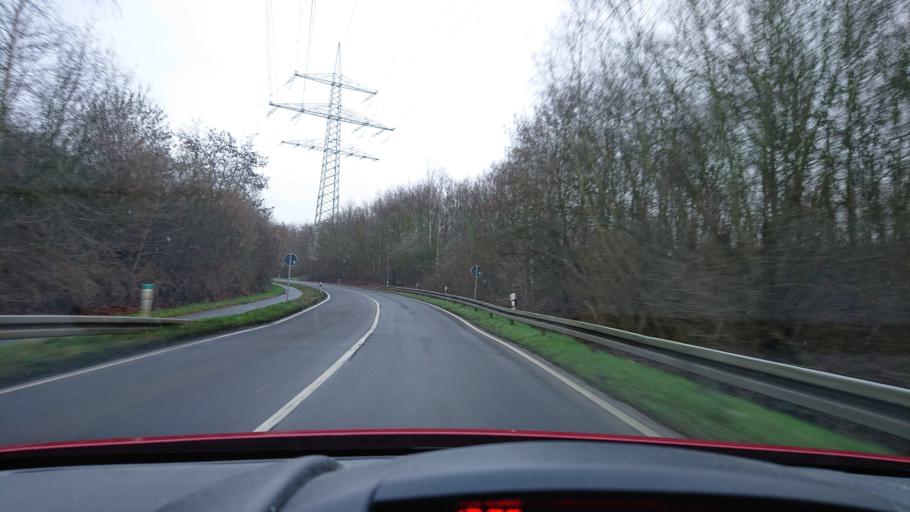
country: DE
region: North Rhine-Westphalia
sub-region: Regierungsbezirk Koln
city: Bergheim
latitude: 50.9670
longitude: 6.6769
